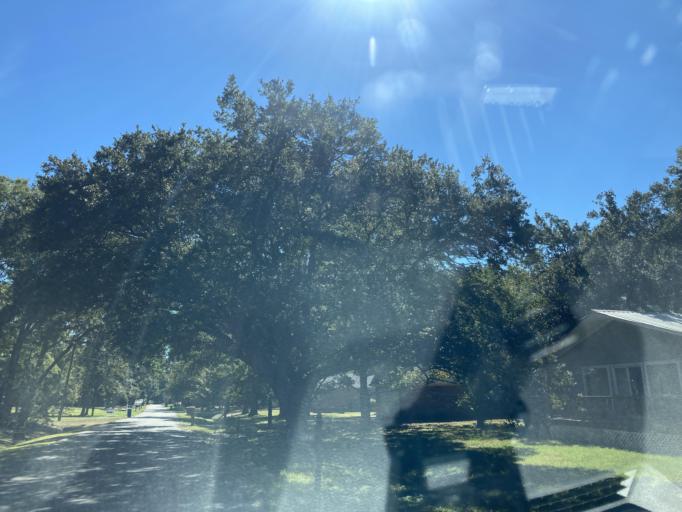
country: US
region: Mississippi
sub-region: Jackson County
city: Ocean Springs
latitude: 30.4092
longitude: -88.8112
